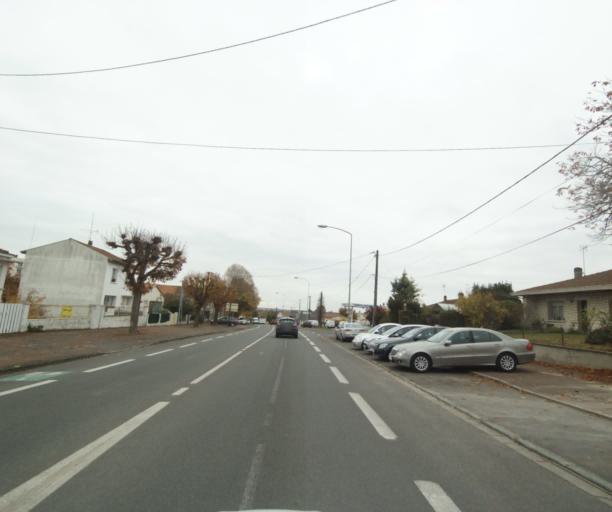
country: FR
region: Poitou-Charentes
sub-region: Departement de la Charente-Maritime
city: Saintes
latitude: 45.7334
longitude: -0.6455
